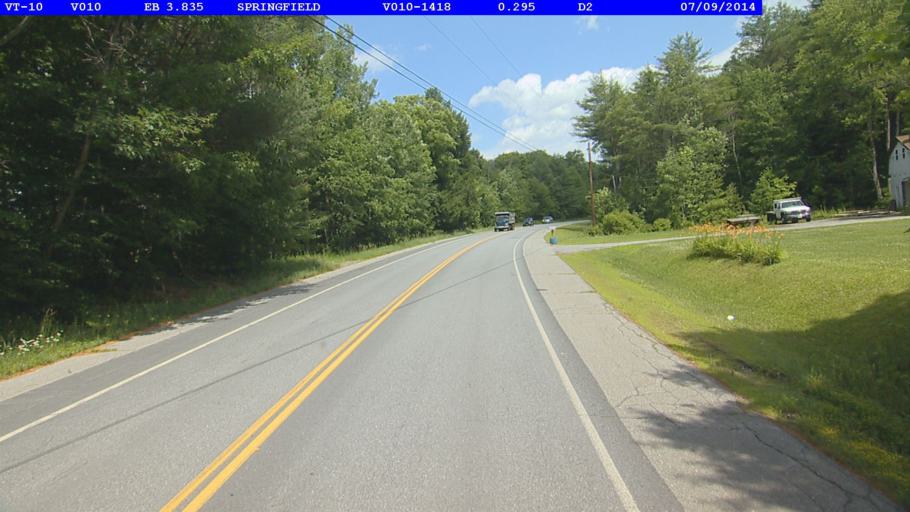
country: US
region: Vermont
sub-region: Windsor County
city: Springfield
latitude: 43.3368
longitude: -72.5413
